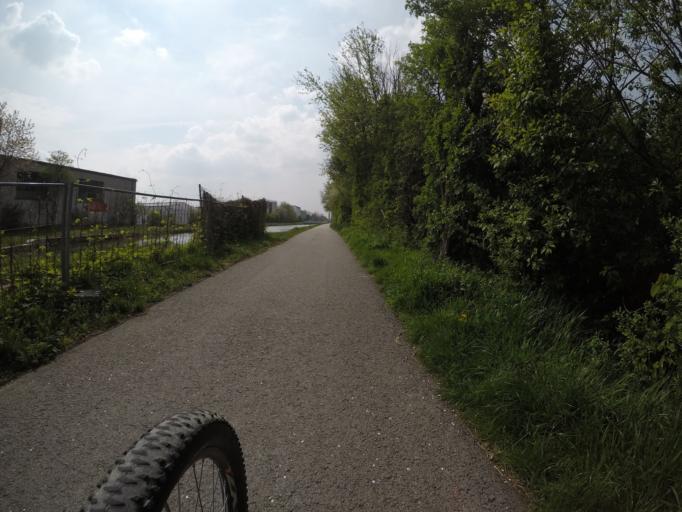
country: AT
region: Lower Austria
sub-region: Politischer Bezirk Modling
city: Gumpoldskirchen
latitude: 48.0341
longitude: 16.2892
